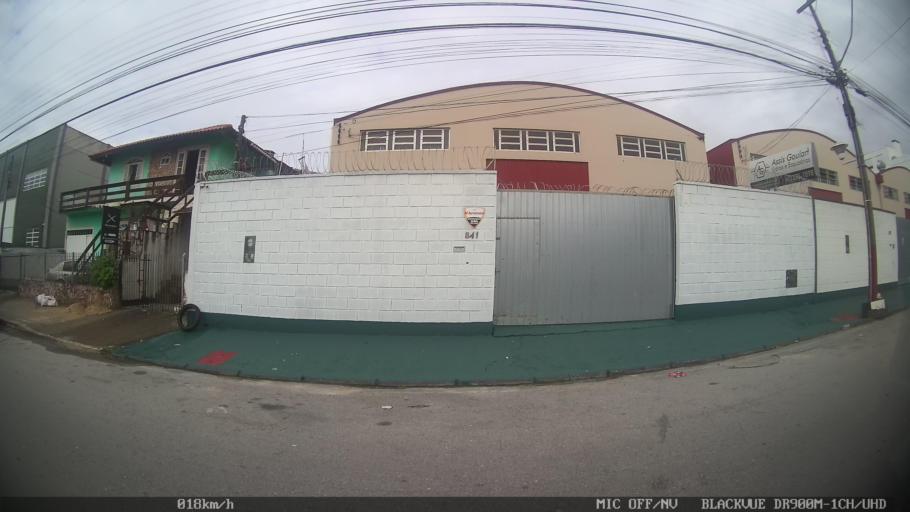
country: BR
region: Santa Catarina
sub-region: Sao Jose
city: Campinas
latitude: -27.5666
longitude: -48.6218
